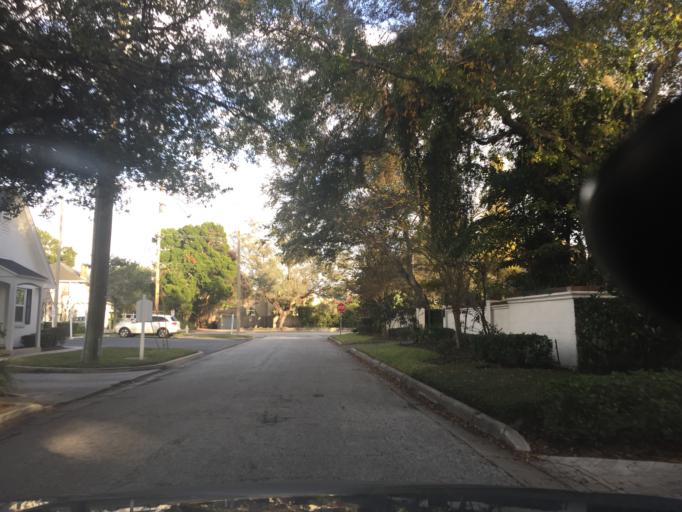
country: US
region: Florida
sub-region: Hillsborough County
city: Tampa
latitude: 27.9333
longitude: -82.4940
